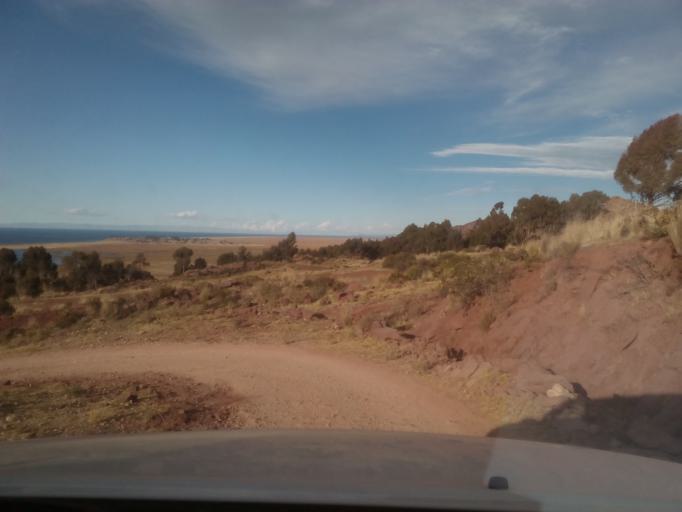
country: PE
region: Puno
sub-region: El Collao
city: Ilave
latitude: -15.9735
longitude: -69.6750
